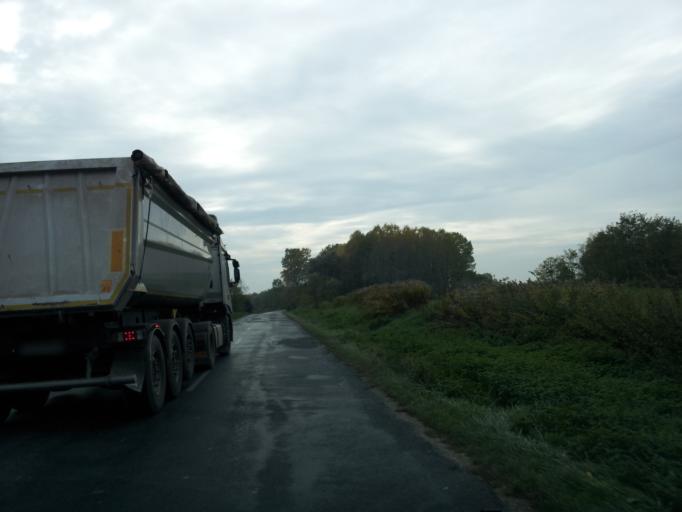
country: HU
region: Gyor-Moson-Sopron
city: Bakonyszentlaszlo
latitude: 47.4362
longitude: 17.7754
